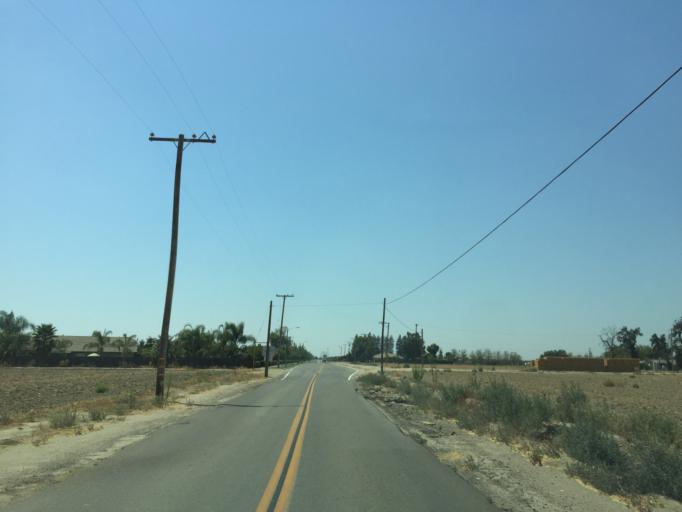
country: US
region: California
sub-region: Tulare County
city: Visalia
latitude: 36.3654
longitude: -119.3177
